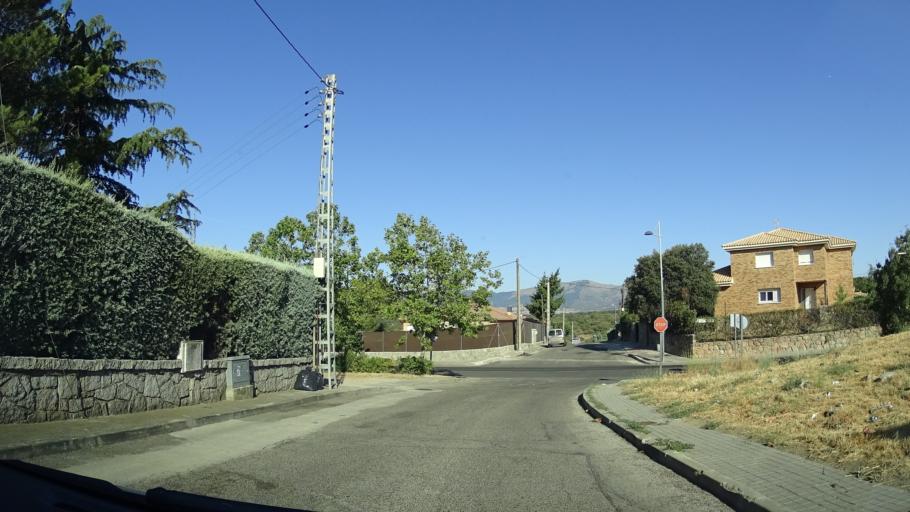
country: ES
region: Madrid
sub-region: Provincia de Madrid
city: Colmenarejo
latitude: 40.5594
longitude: -4.0213
